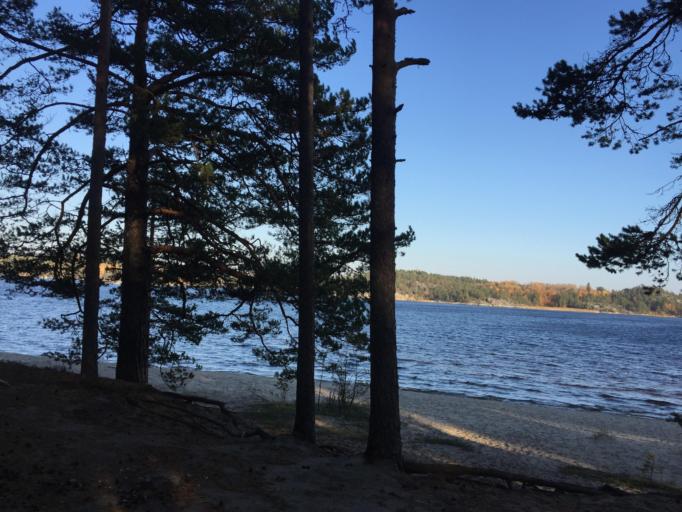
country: RU
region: Republic of Karelia
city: Lakhdenpokh'ya
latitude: 61.2859
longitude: 30.1357
